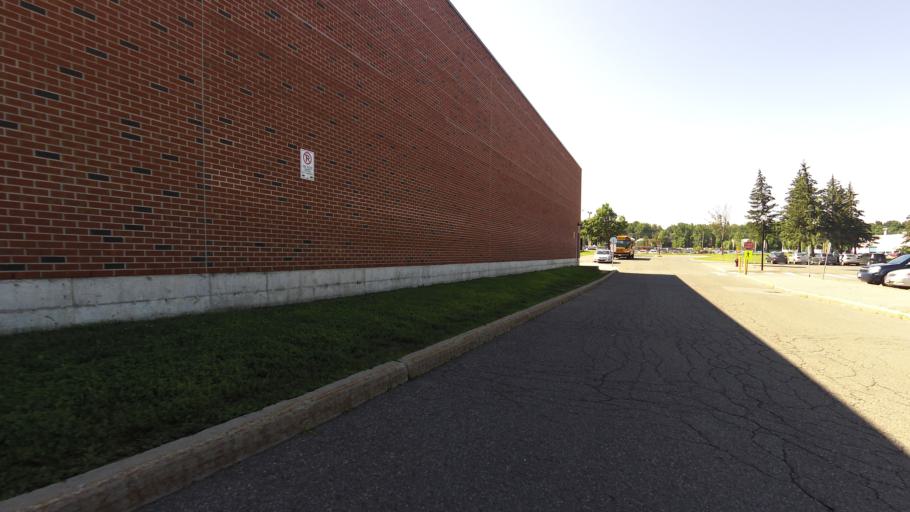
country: CA
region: Quebec
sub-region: Outaouais
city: Gatineau
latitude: 45.4665
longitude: -75.5456
